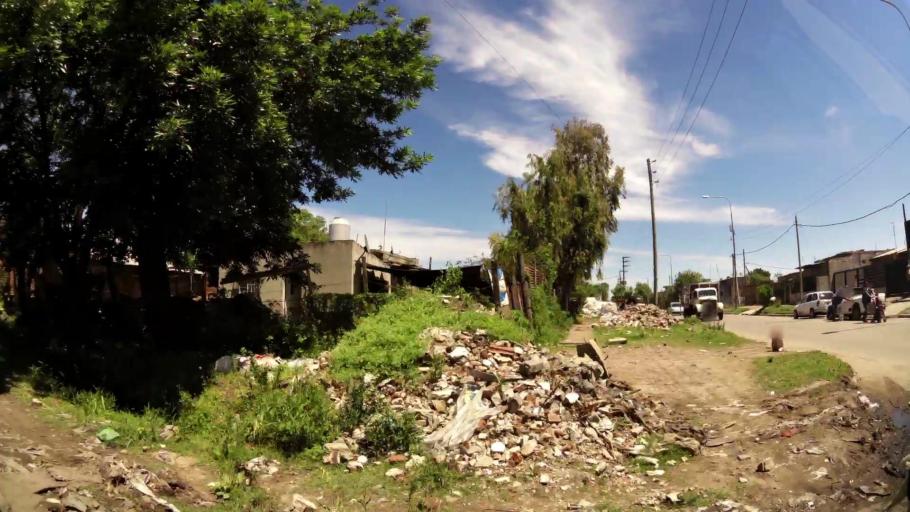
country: AR
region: Buenos Aires
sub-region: Partido de Quilmes
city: Quilmes
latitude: -34.7419
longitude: -58.3071
